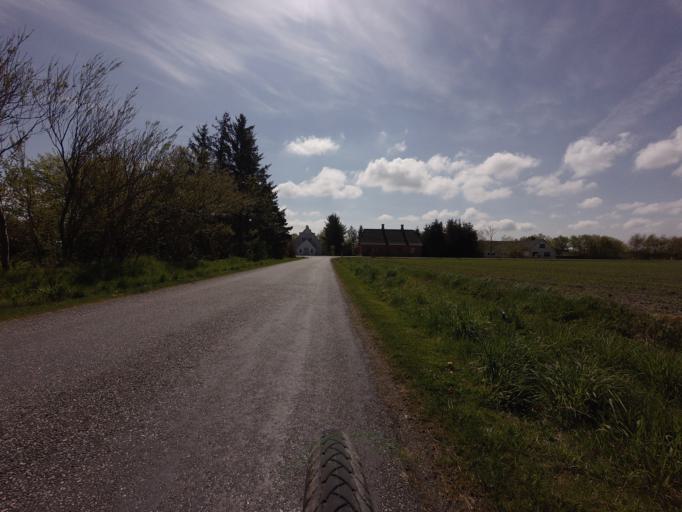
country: DK
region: North Denmark
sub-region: Jammerbugt Kommune
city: Brovst
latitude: 57.1477
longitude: 9.5536
